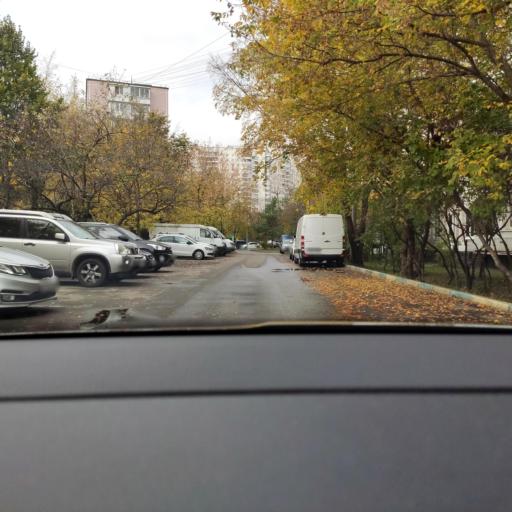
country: RU
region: Moscow
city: Strogino
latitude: 55.8130
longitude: 37.4037
